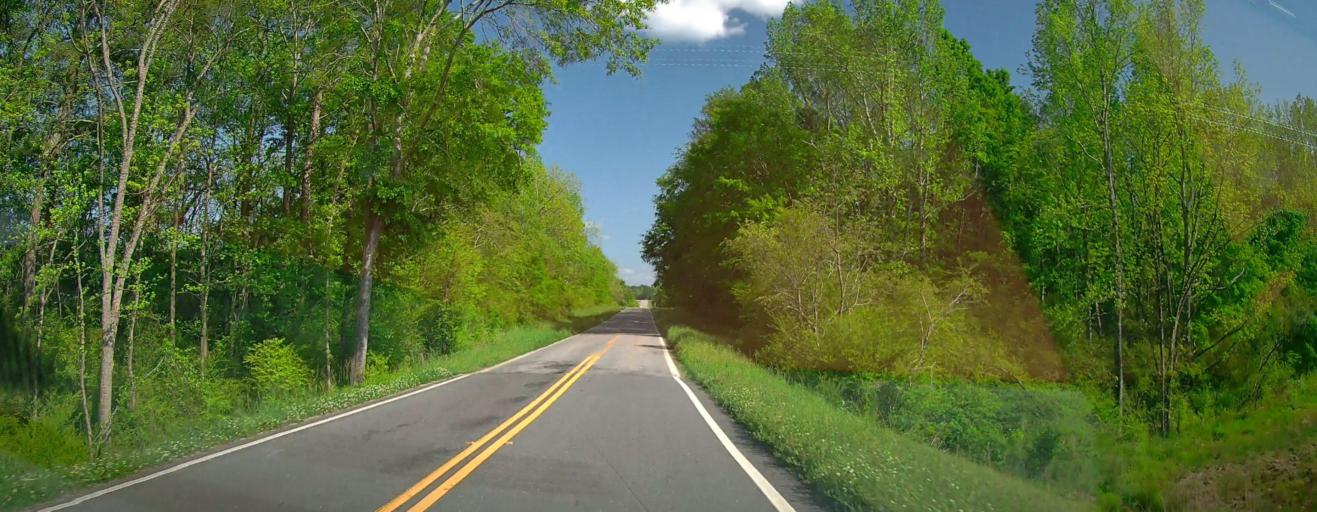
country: US
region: Georgia
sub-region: Morgan County
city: Madison
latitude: 33.5626
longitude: -83.4941
